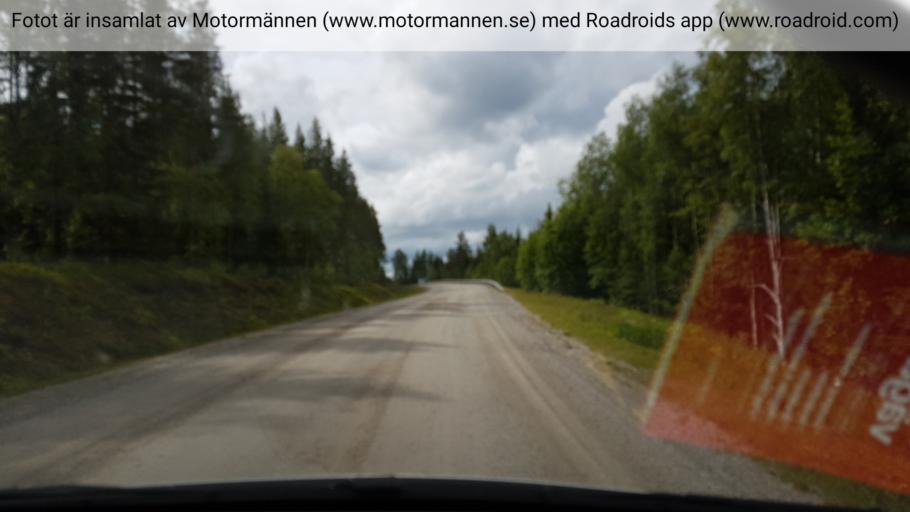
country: SE
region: Vaesternorrland
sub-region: Solleftea Kommun
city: Solleftea
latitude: 63.3835
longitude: 17.4994
